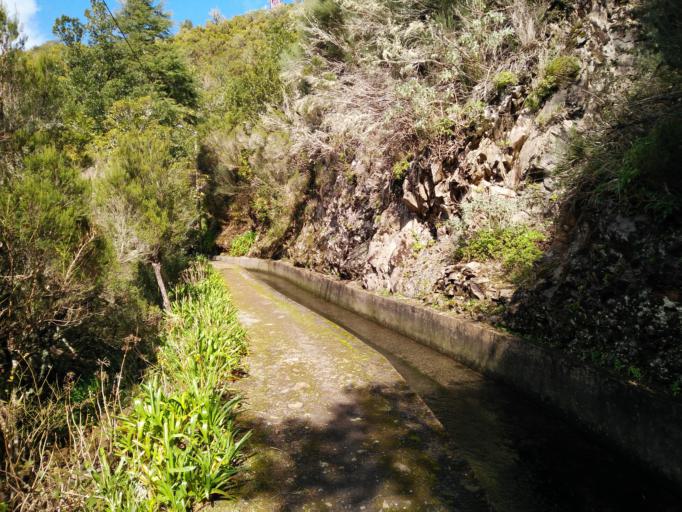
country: PT
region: Madeira
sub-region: Sao Vicente
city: Sao Vicente
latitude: 32.7528
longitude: -17.0177
